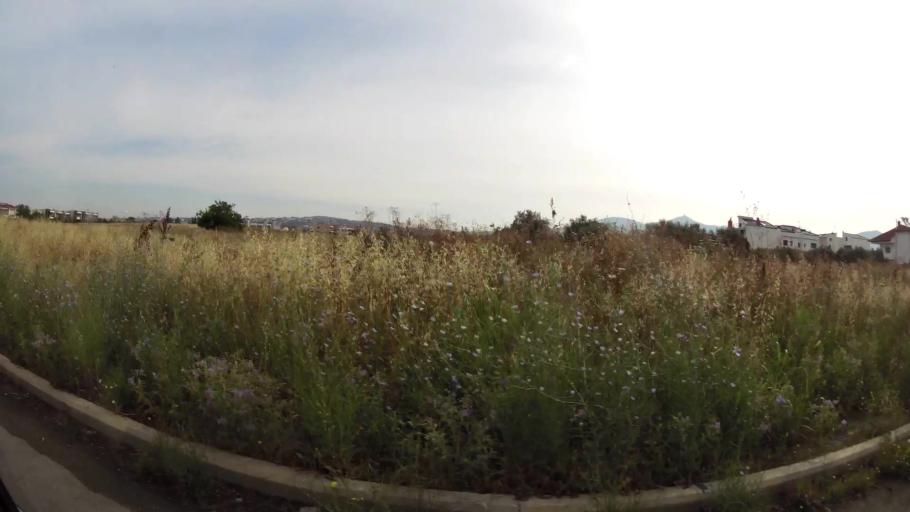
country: GR
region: Central Macedonia
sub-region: Nomos Thessalonikis
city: Thermi
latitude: 40.5488
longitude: 23.0116
